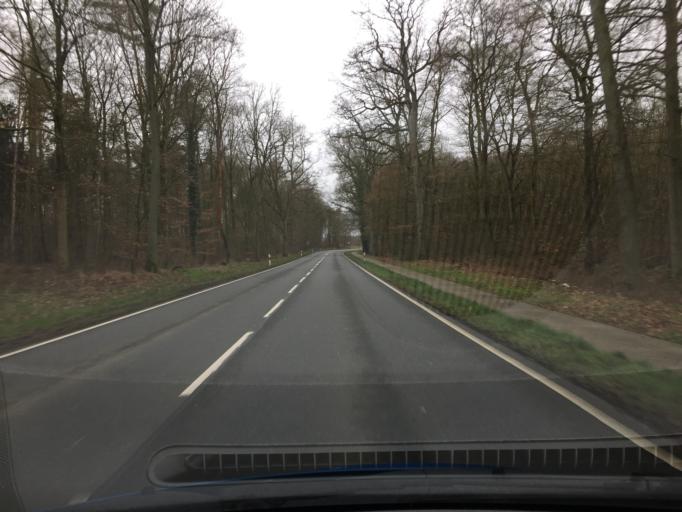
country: DE
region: Lower Saxony
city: Uelzen
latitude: 52.9752
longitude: 10.6046
